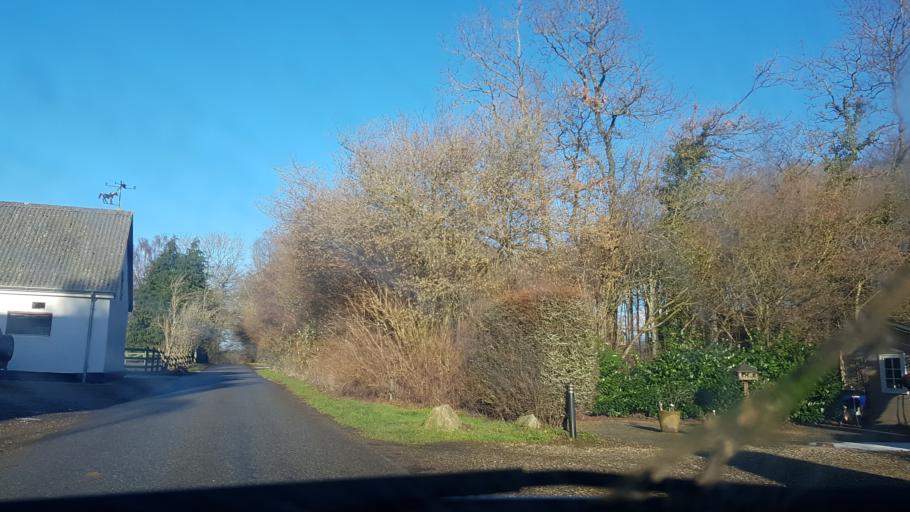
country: DK
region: South Denmark
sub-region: Fredericia Kommune
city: Taulov
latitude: 55.5220
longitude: 9.6516
